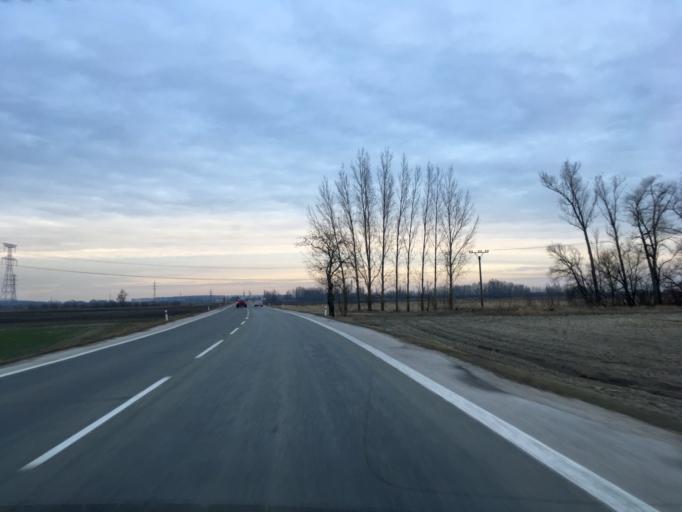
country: SK
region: Trnavsky
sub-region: Okres Dunajska Streda
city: Velky Meder
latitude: 47.8876
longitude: 17.7431
